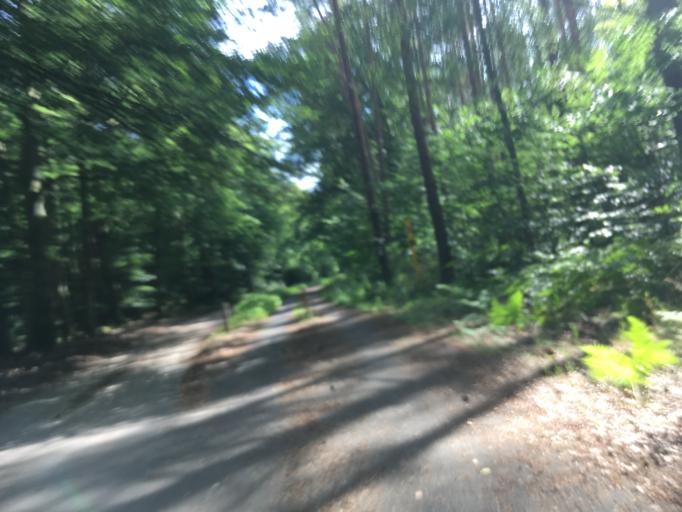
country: DE
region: Brandenburg
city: Rheinsberg
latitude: 53.0718
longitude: 12.9078
